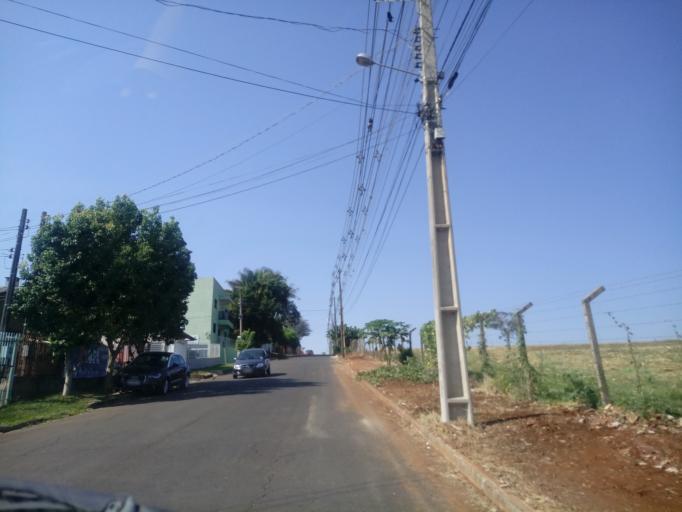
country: BR
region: Santa Catarina
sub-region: Chapeco
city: Chapeco
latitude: -27.0827
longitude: -52.6353
